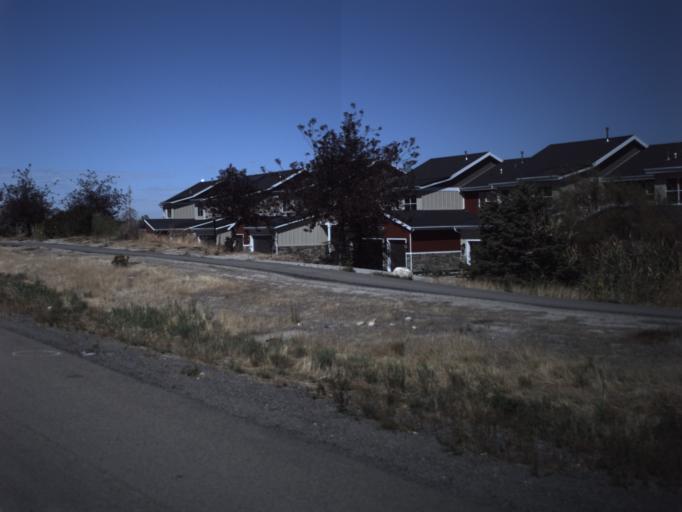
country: US
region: Utah
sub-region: Utah County
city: Saratoga Springs
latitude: 40.3190
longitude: -111.8997
